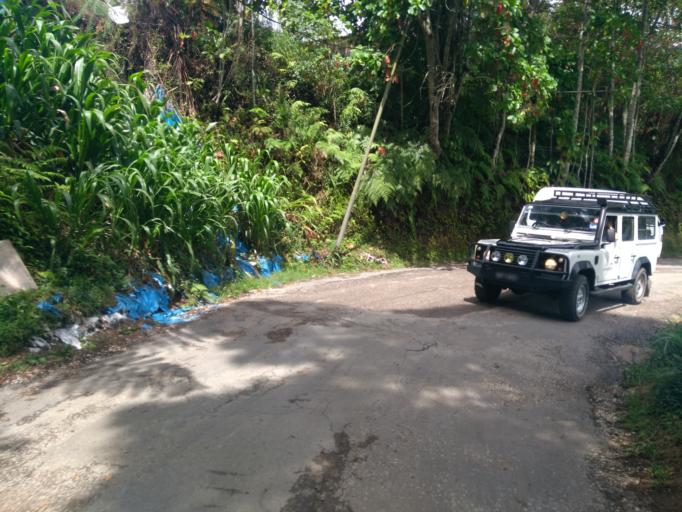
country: MY
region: Pahang
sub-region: Cameron Highlands
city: Tanah Rata
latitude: 4.5155
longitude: 101.4155
